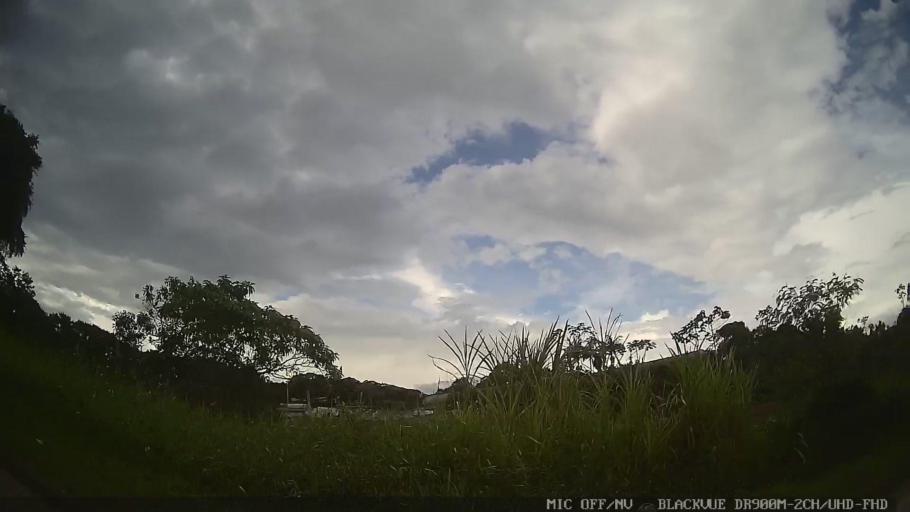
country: BR
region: Sao Paulo
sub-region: Biritiba-Mirim
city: Biritiba Mirim
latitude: -23.5520
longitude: -45.9701
